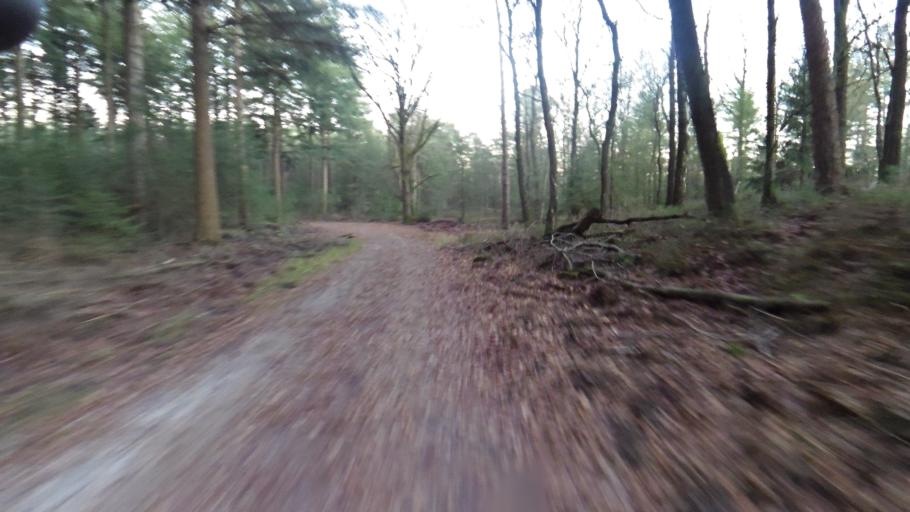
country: NL
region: Gelderland
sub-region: Gemeente Apeldoorn
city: Uddel
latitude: 52.2113
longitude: 5.8207
